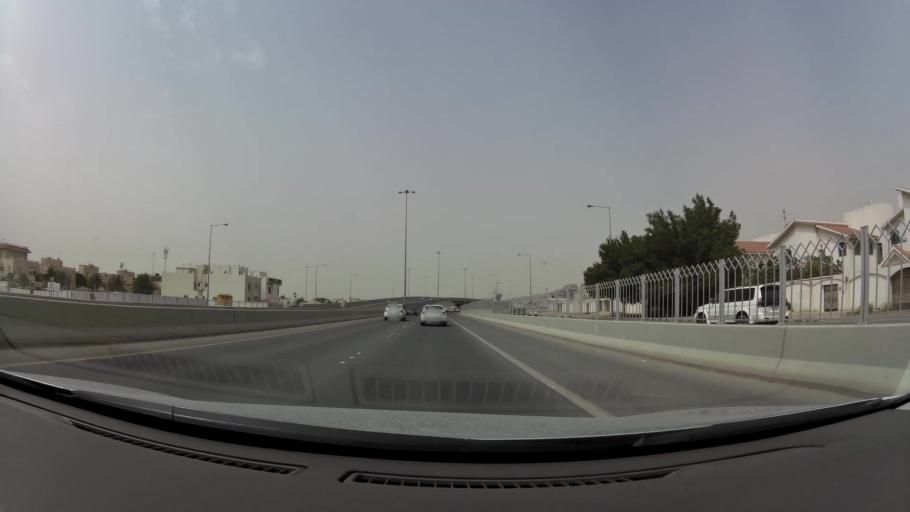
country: QA
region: Baladiyat ad Dawhah
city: Doha
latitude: 25.2545
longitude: 51.5110
